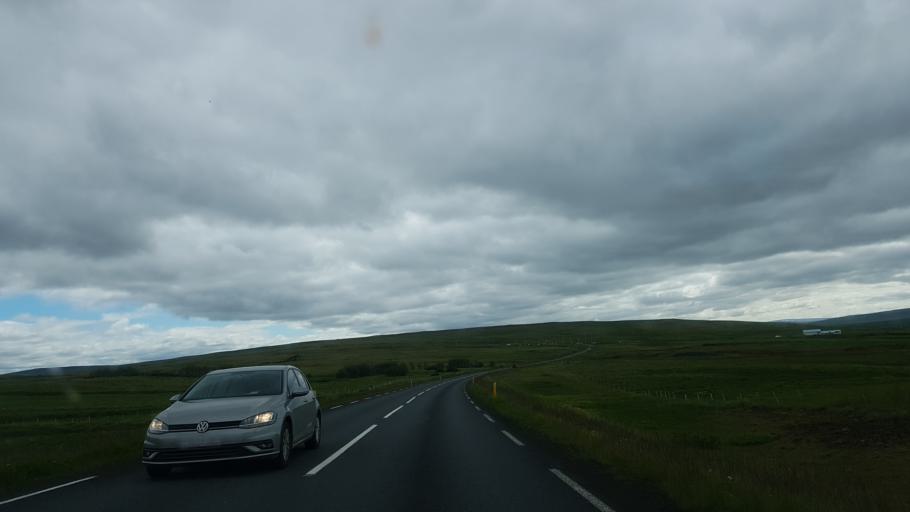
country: IS
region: Northwest
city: Saudarkrokur
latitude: 65.3611
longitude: -20.8926
